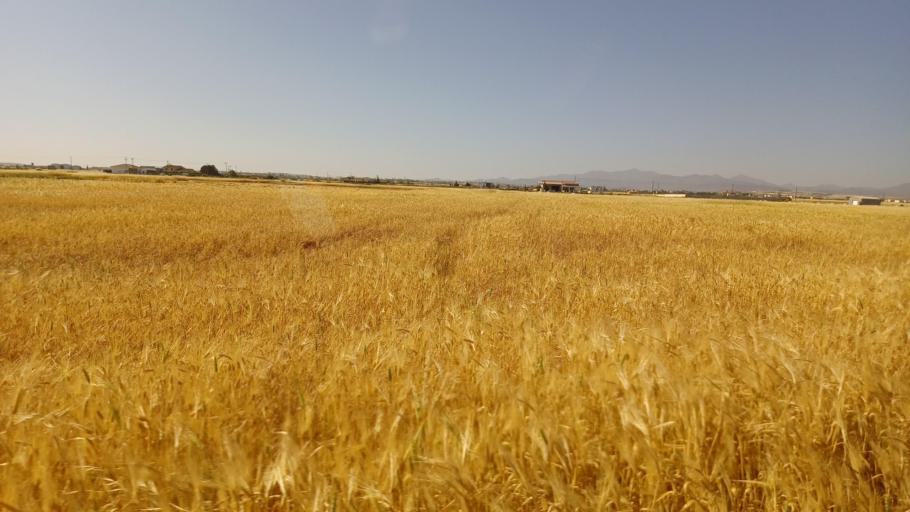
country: CY
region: Lefkosia
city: Kokkinotrimithia
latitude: 35.1430
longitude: 33.2234
